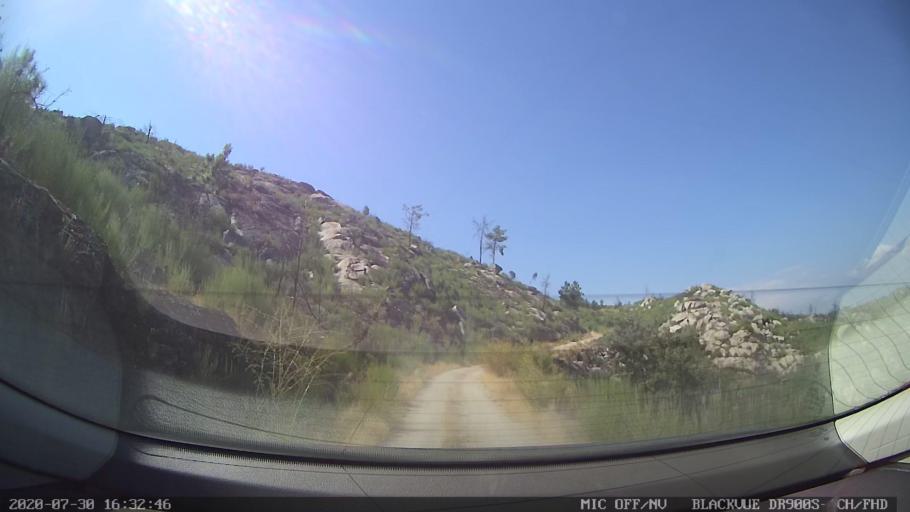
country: PT
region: Vila Real
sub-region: Sabrosa
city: Sabrosa
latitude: 41.3109
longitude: -7.4918
